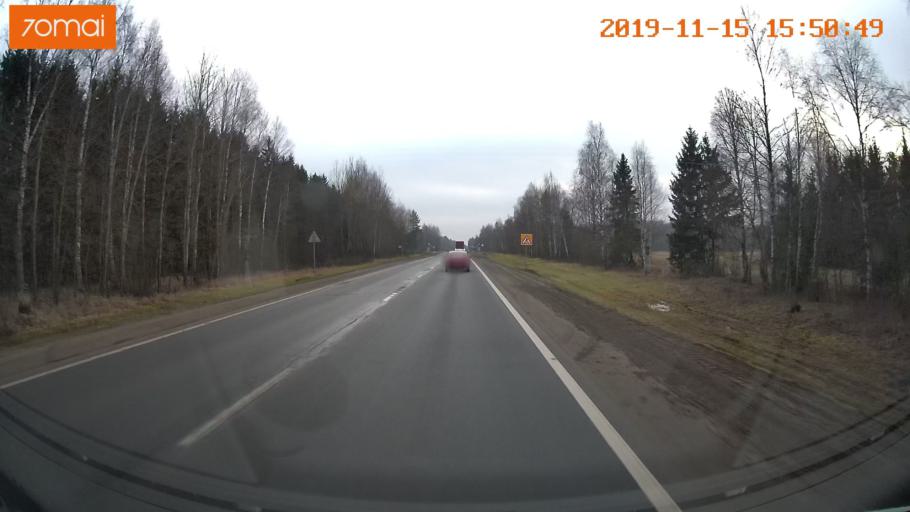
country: RU
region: Jaroslavl
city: Yaroslavl
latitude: 57.9015
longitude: 40.0119
